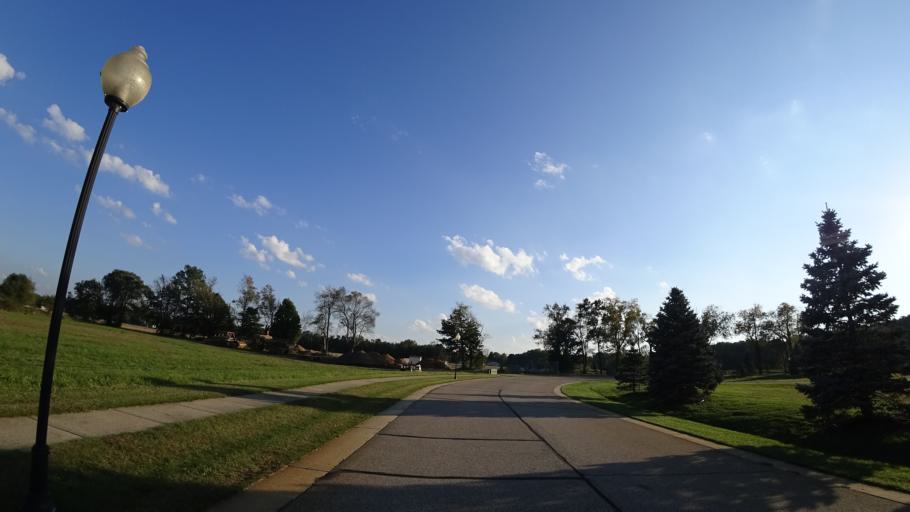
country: US
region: Michigan
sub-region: Saint Joseph County
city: Three Rivers
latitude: 41.9654
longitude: -85.6302
